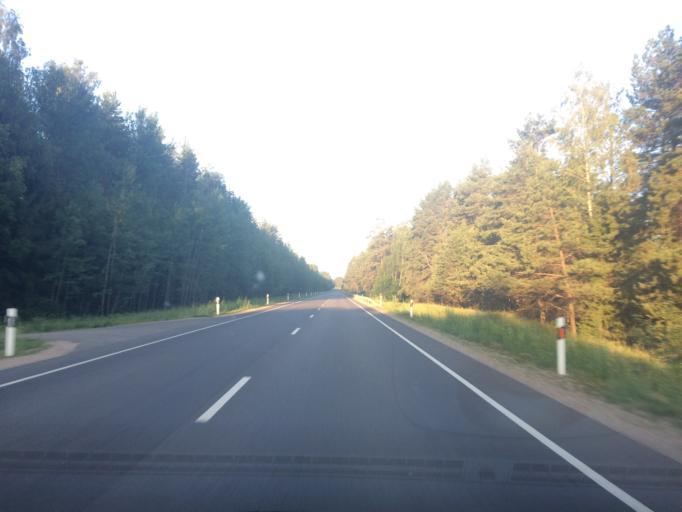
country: LT
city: Zarasai
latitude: 55.6841
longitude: 26.1256
